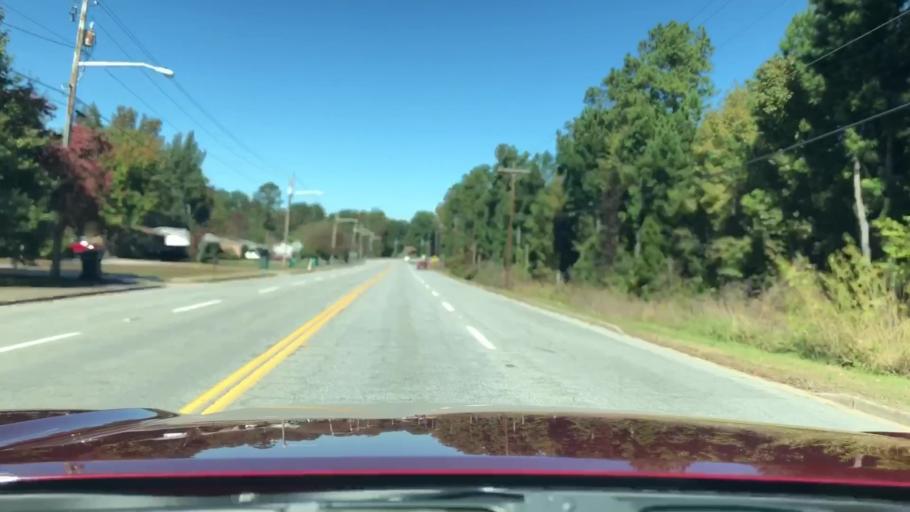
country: US
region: South Carolina
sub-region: Greenwood County
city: Greenwood
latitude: 34.2205
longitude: -82.1393
